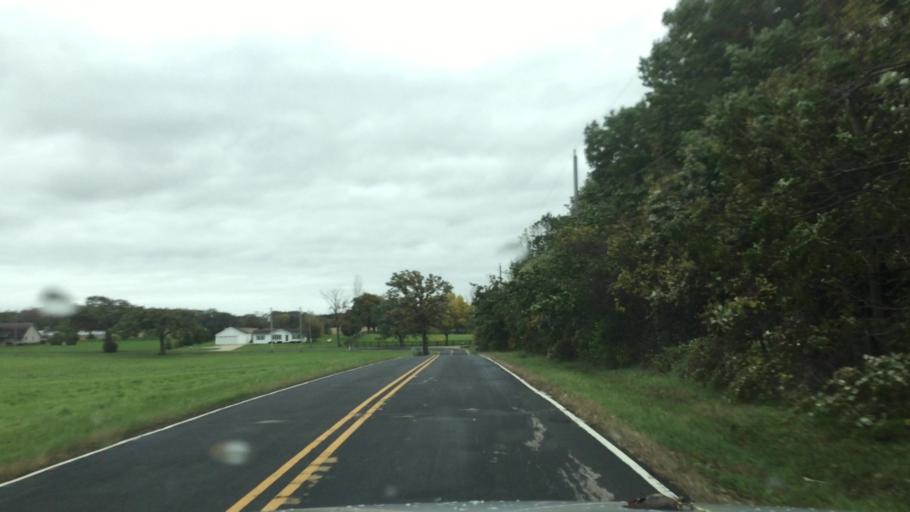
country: US
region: Wisconsin
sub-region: Racine County
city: Waterford
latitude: 42.7590
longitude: -88.1607
